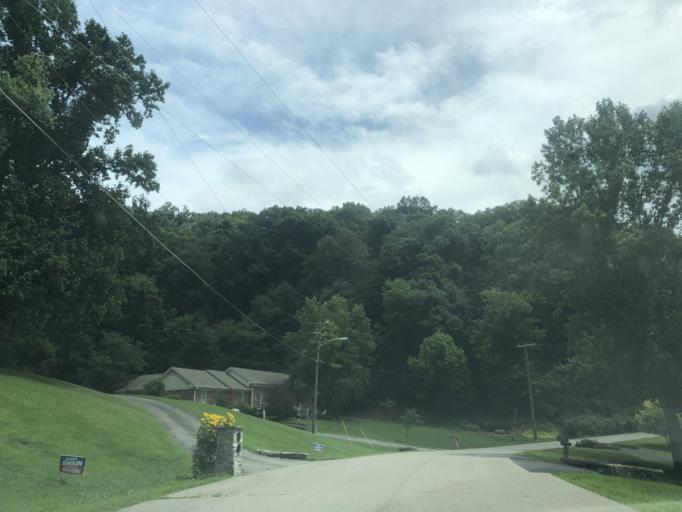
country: US
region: Tennessee
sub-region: Davidson County
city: Oak Hill
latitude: 36.0687
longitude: -86.8075
